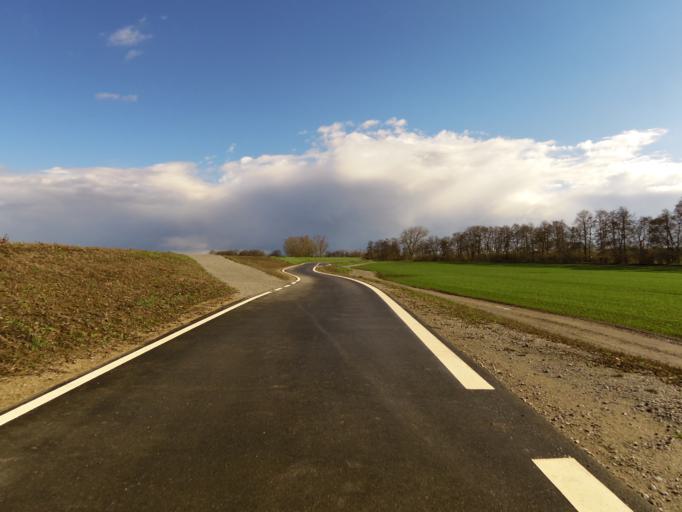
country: DE
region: Hesse
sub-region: Regierungsbezirk Darmstadt
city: Biblis
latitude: 49.6798
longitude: 8.4205
